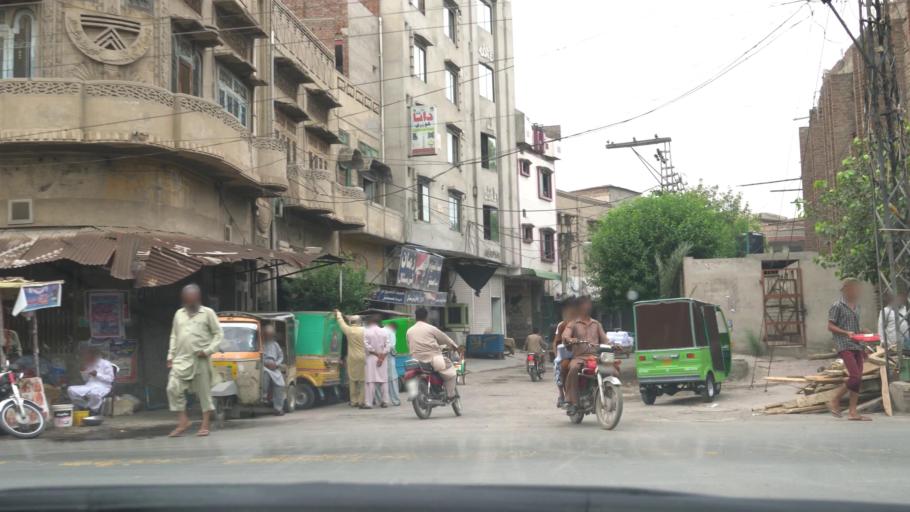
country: PK
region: Punjab
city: Faisalabad
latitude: 31.4213
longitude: 73.0677
